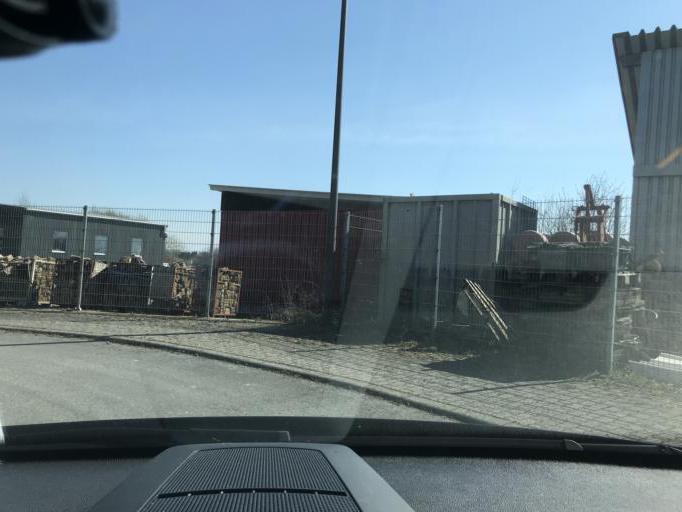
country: DE
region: Rheinland-Pfalz
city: Trierweiler
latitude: 49.7736
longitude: 6.5784
